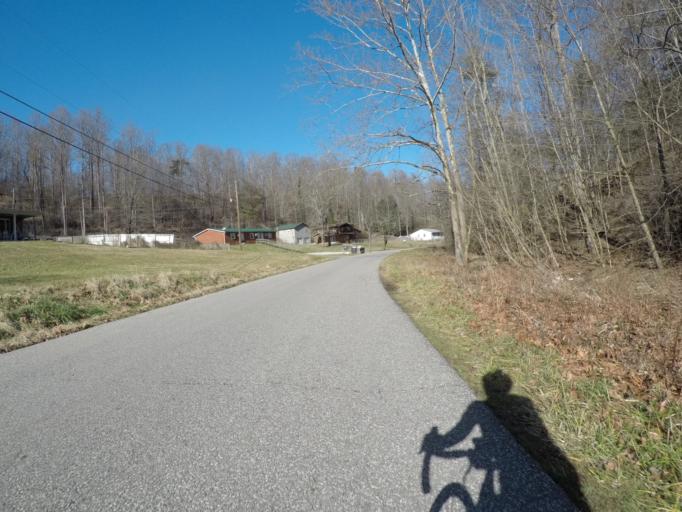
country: US
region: Kentucky
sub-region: Boyd County
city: Catlettsburg
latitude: 38.4171
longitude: -82.6408
